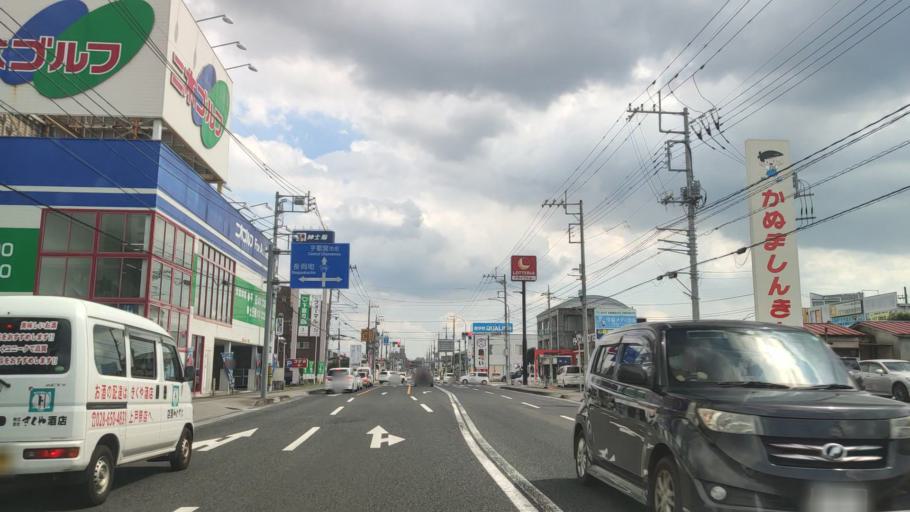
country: JP
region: Tochigi
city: Utsunomiya-shi
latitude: 36.5866
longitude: 139.8656
